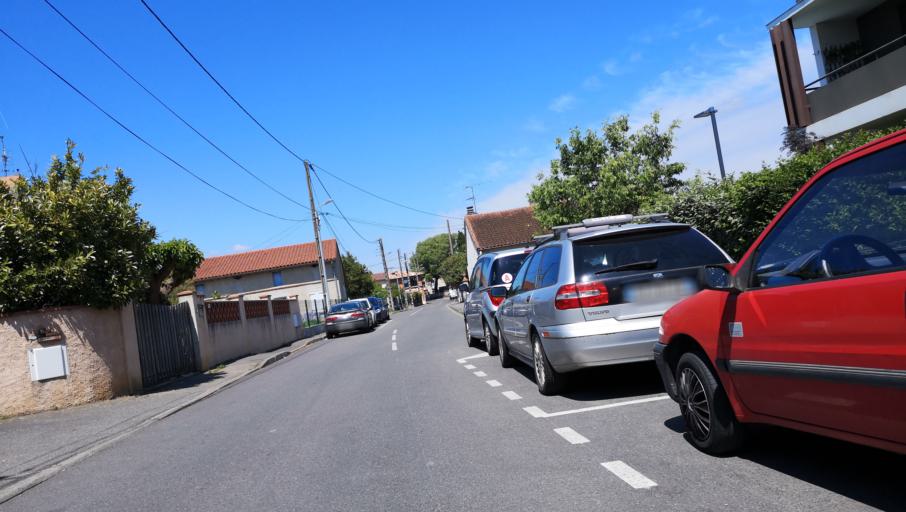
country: FR
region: Midi-Pyrenees
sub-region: Departement de la Haute-Garonne
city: Blagnac
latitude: 43.6392
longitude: 1.3909
